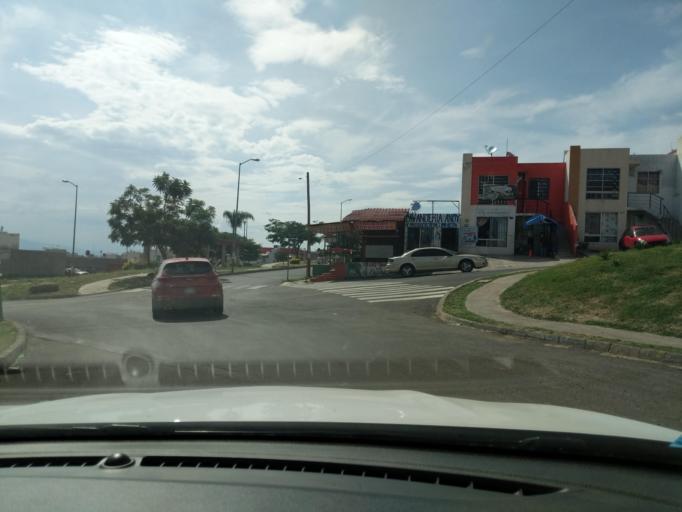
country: MX
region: Jalisco
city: San Jose del Castillo
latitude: 20.5213
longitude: -103.2294
